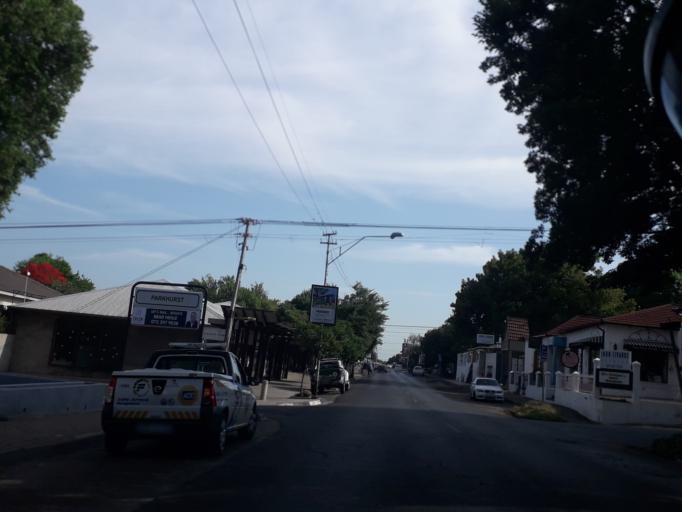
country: ZA
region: Gauteng
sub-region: City of Johannesburg Metropolitan Municipality
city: Johannesburg
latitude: -26.1419
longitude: 28.0169
